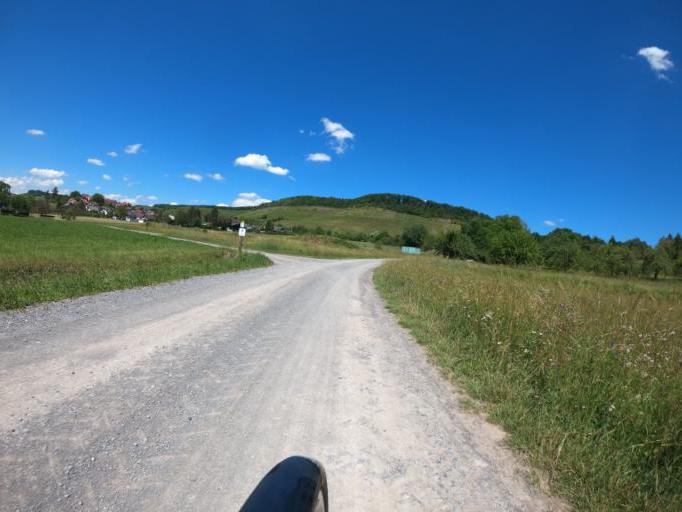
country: DE
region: Baden-Wuerttemberg
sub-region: Regierungsbezirk Stuttgart
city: Cleebronn
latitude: 49.0139
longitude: 9.0052
